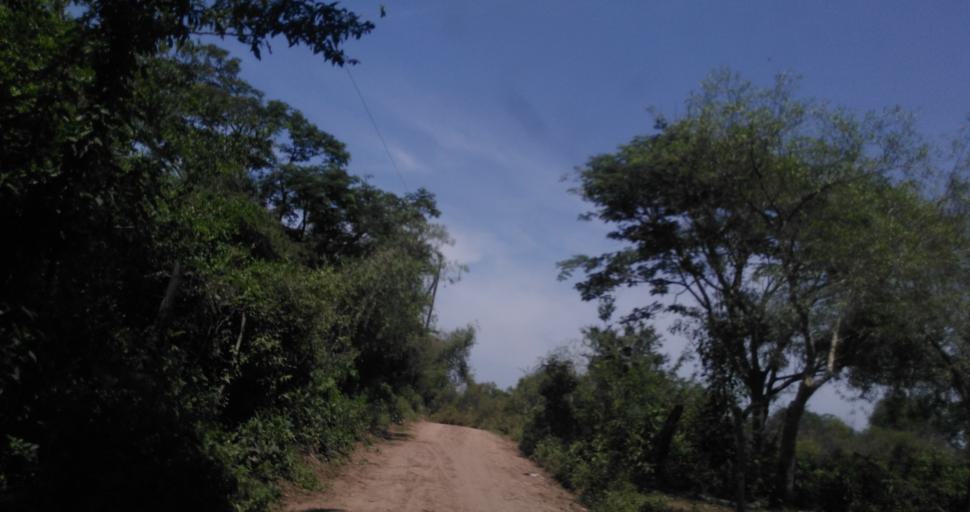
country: AR
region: Chaco
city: Fontana
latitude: -27.4114
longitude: -59.0132
